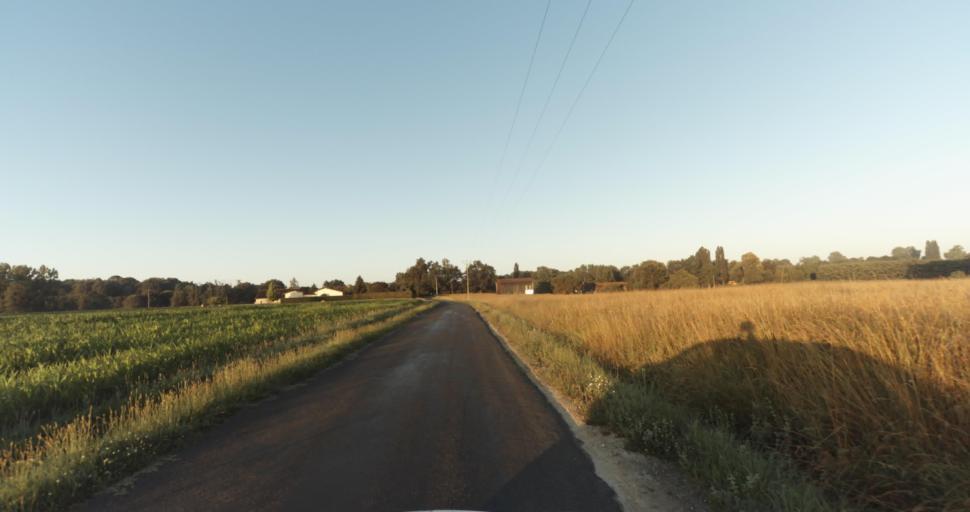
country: FR
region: Aquitaine
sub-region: Departement de la Gironde
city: Bazas
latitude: 44.4269
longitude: -0.2052
